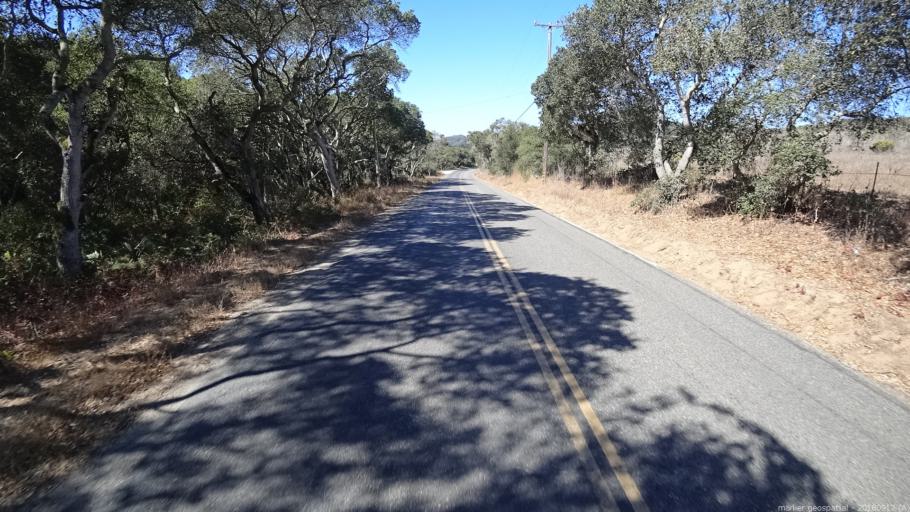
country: US
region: California
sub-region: Monterey County
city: Elkhorn
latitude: 36.8324
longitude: -121.6910
